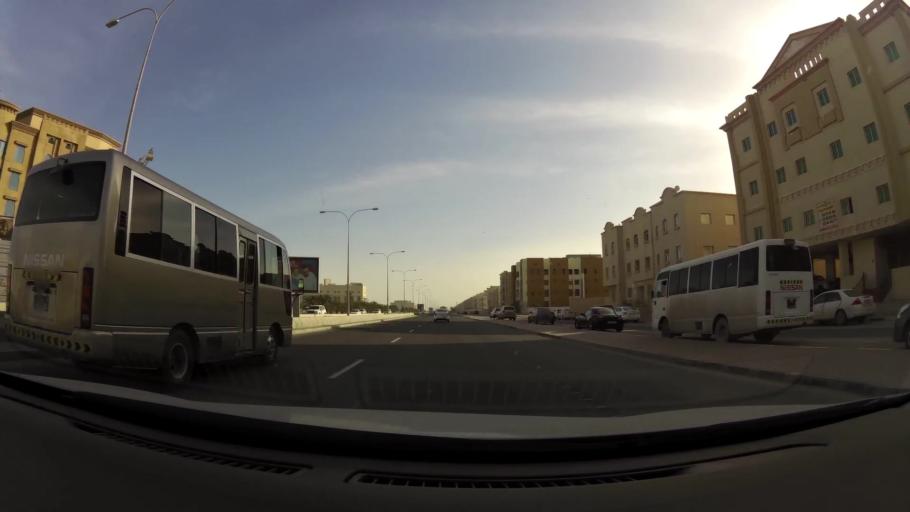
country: QA
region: Al Wakrah
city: Al Wakrah
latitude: 25.1594
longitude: 51.6063
